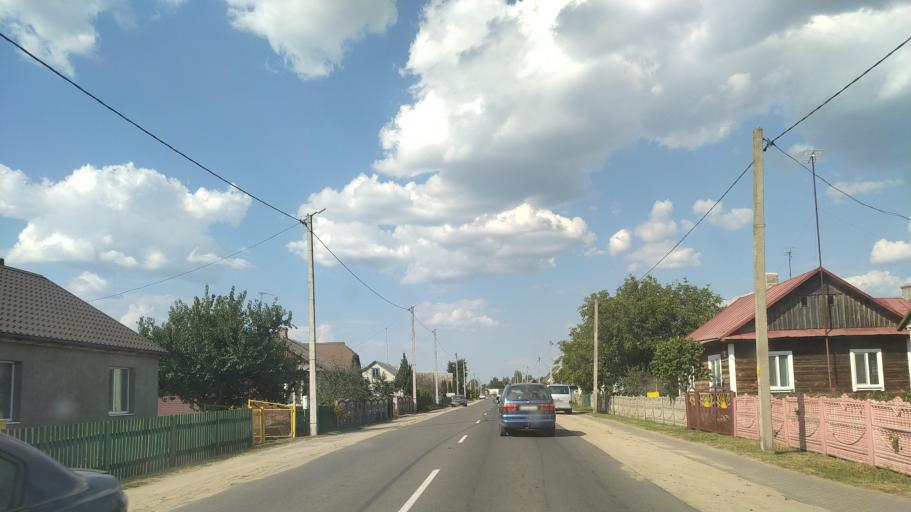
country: BY
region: Brest
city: Drahichyn
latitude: 52.1956
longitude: 25.1477
